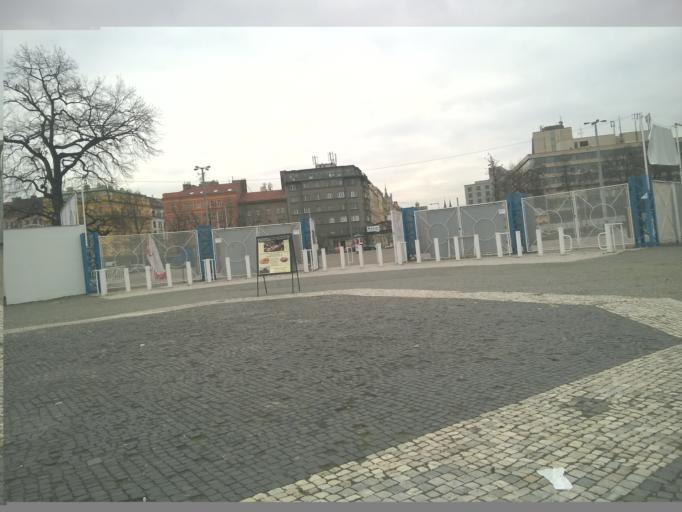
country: CZ
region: Praha
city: Prague
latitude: 50.1050
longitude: 14.4309
